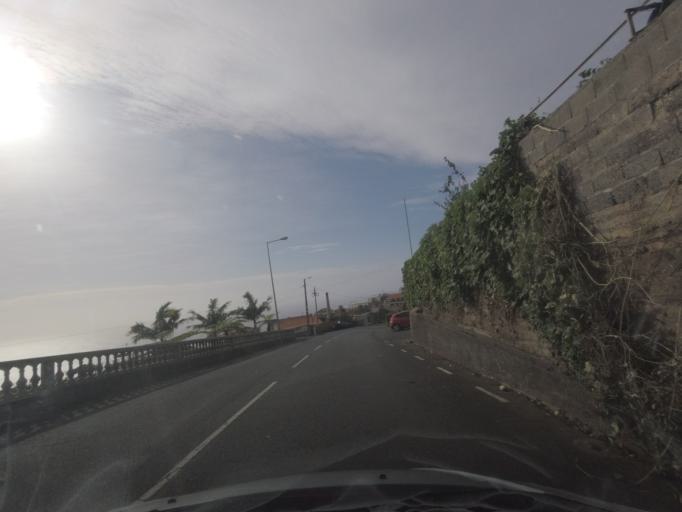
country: PT
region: Madeira
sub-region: Calheta
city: Estreito da Calheta
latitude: 32.7347
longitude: -17.1886
